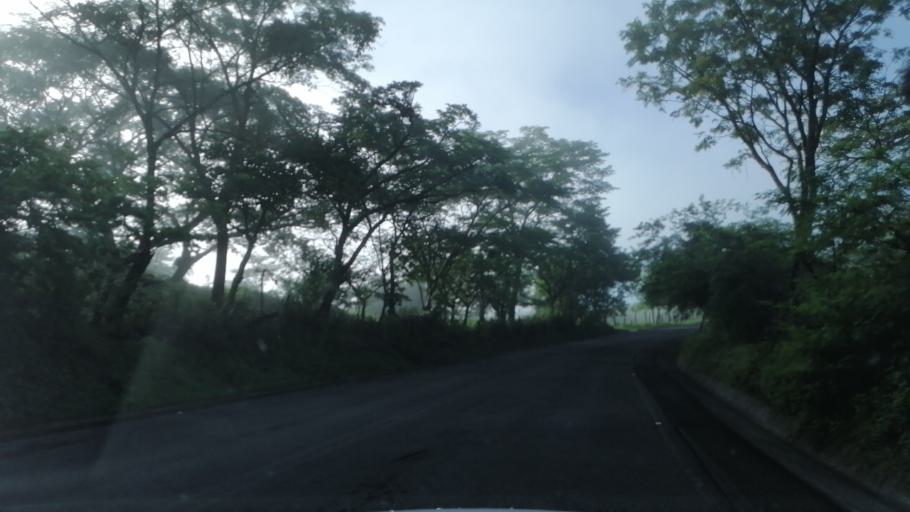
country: SV
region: Morazan
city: Cacaopera
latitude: 13.7889
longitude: -88.1120
